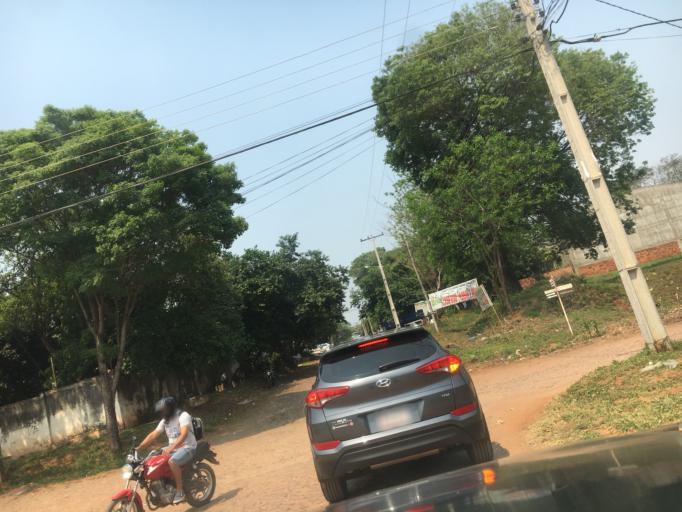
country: PY
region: Central
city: Villa Elisa
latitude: -25.3623
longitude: -57.5906
